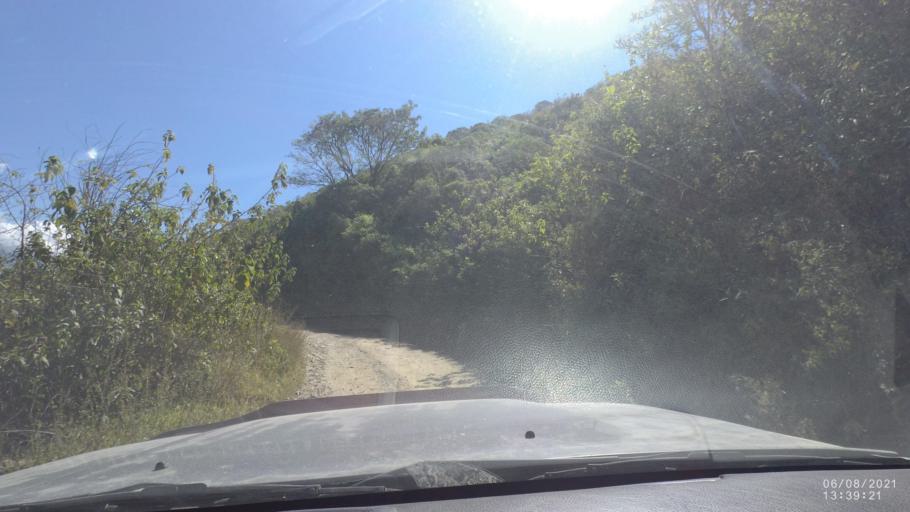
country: BO
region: La Paz
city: Quime
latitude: -16.6859
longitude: -66.7280
